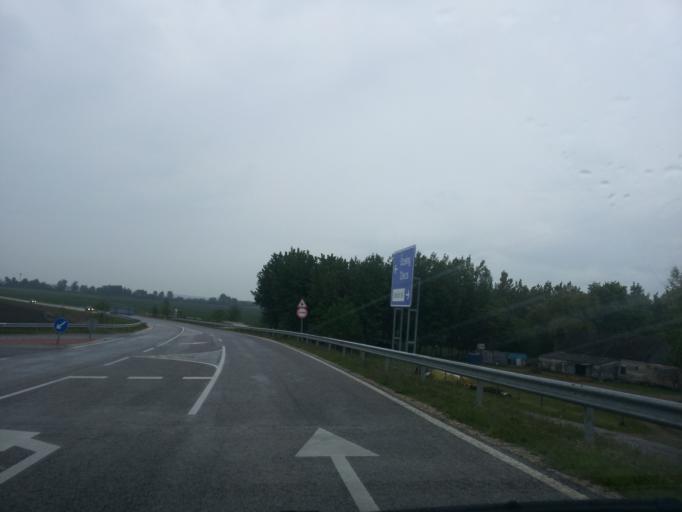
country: HU
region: Tolna
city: Ocseny
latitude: 46.3079
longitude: 18.7263
